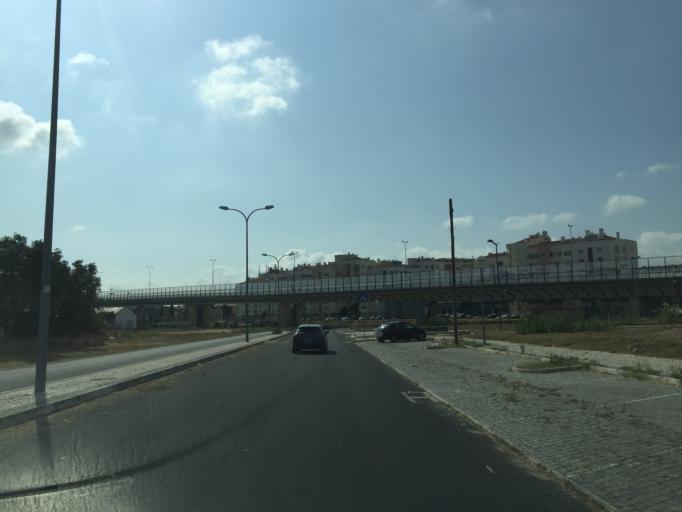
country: PT
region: Lisbon
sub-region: Odivelas
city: Olival do Basto
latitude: 38.7756
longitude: -9.1580
